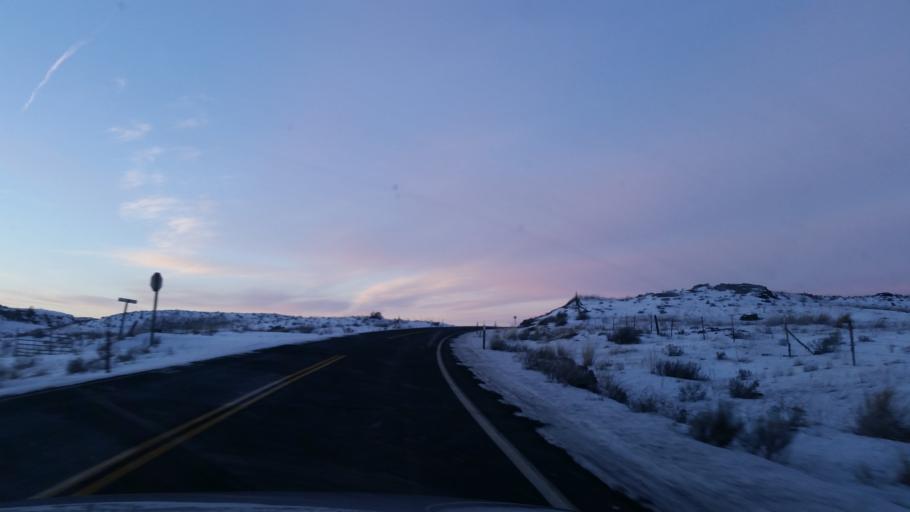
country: US
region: Washington
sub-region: Spokane County
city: Medical Lake
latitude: 47.2742
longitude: -117.9536
